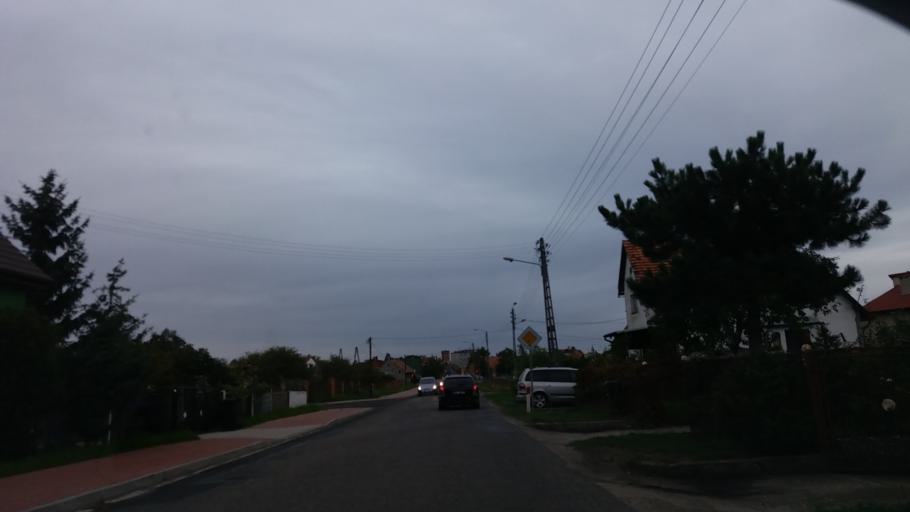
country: PL
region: Lower Silesian Voivodeship
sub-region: Powiat legnicki
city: Prochowice
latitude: 51.2688
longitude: 16.3649
